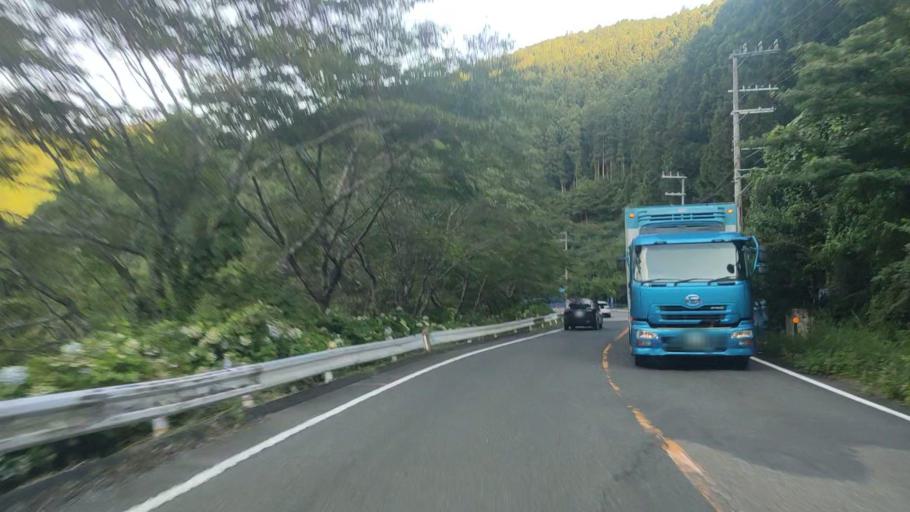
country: JP
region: Wakayama
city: Tanabe
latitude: 33.8173
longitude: 135.5565
